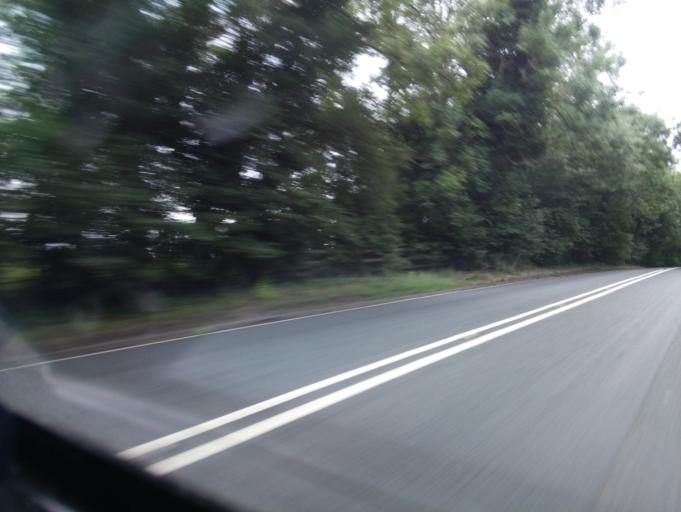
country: GB
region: England
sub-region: Worcestershire
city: Droitwich
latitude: 52.2818
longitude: -2.1286
